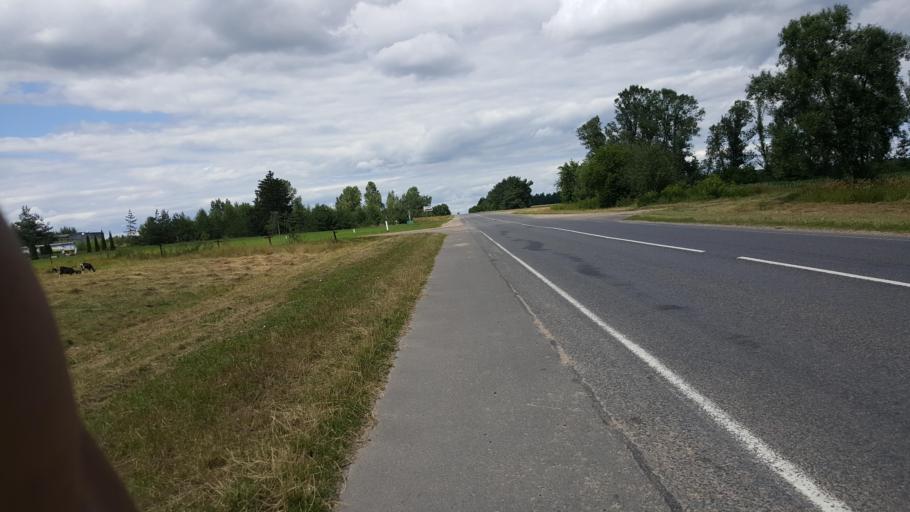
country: BY
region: Brest
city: Kamyanyets
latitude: 52.3342
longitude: 23.9119
